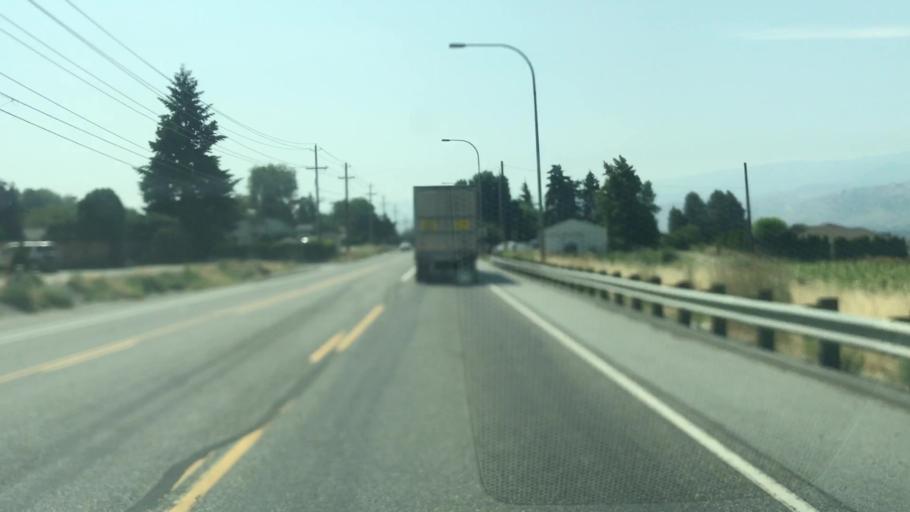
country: US
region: Washington
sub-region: Douglas County
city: East Wenatchee Bench
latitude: 47.4601
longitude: -120.2974
